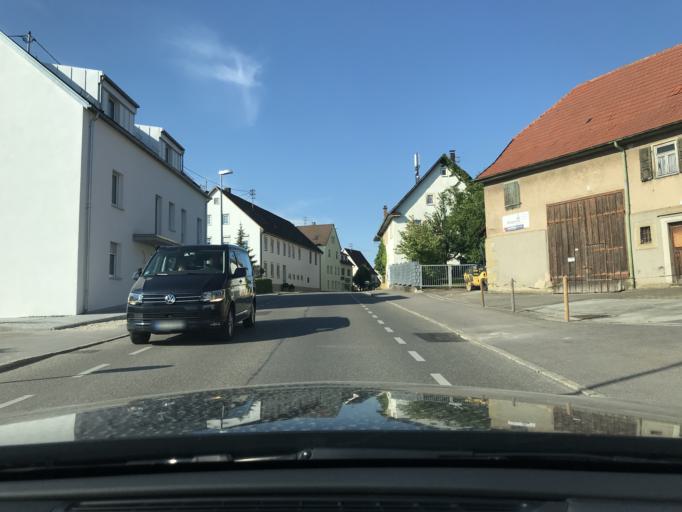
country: DE
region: Baden-Wuerttemberg
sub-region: Regierungsbezirk Stuttgart
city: Waiblingen
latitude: 48.8488
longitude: 9.3219
